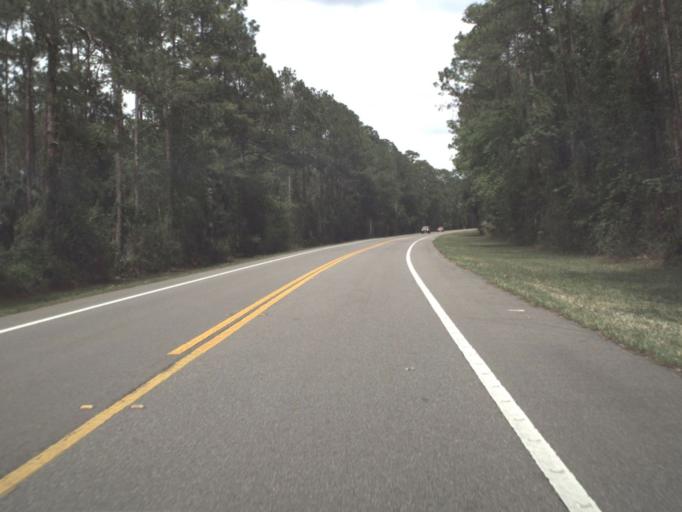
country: US
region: Florida
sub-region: Flagler County
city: Bunnell
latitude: 29.4248
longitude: -81.2979
